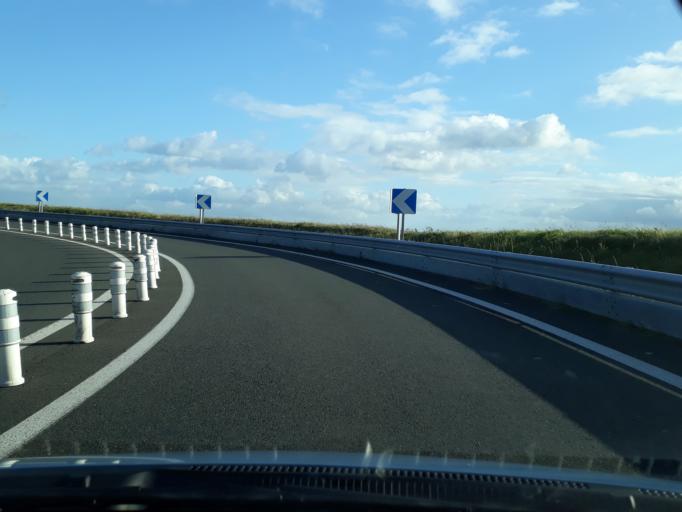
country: FR
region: Centre
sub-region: Departement du Loiret
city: Pithiviers-le-Vieil
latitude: 48.1140
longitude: 2.1944
